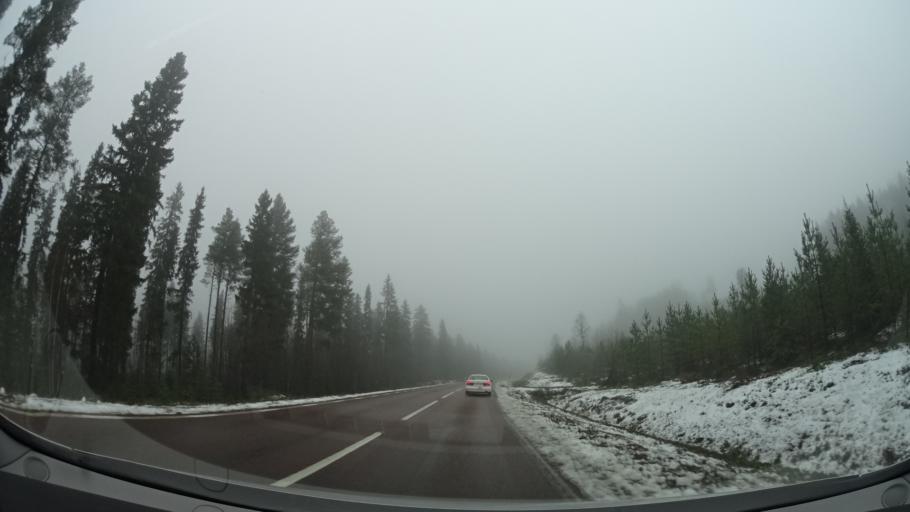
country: SE
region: Vaesterbotten
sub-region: Dorotea Kommun
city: Dorotea
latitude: 64.1455
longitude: 16.2375
